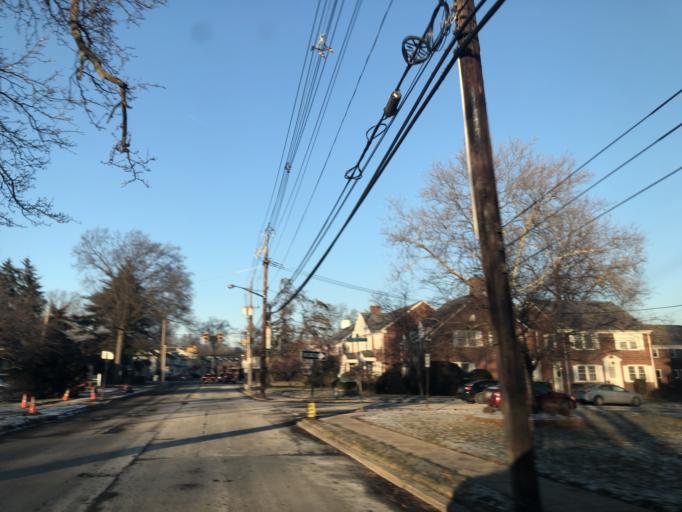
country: US
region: New Jersey
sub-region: Essex County
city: Irvington
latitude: 40.7257
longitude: -74.2515
